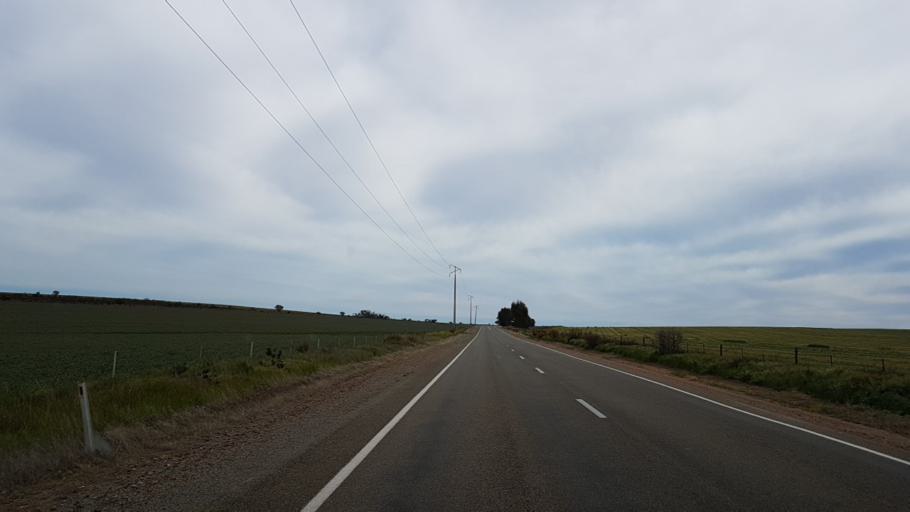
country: AU
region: South Australia
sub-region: Port Pirie City and Dists
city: Crystal Brook
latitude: -33.2766
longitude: 138.3019
